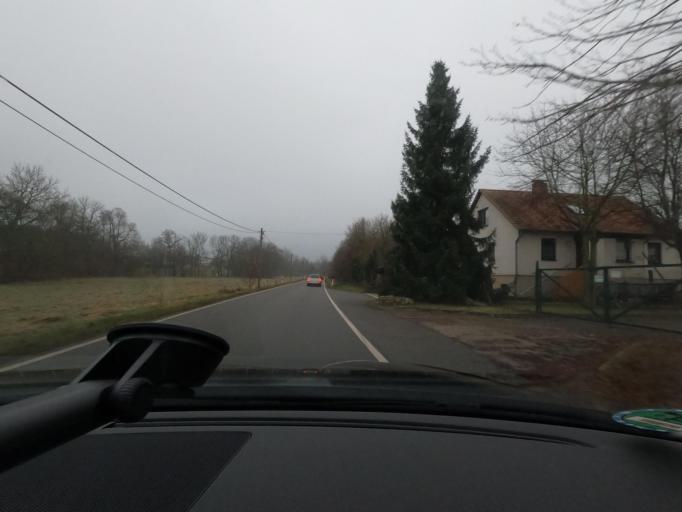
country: DE
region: Thuringia
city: Dornheim
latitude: 50.8151
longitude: 11.0106
